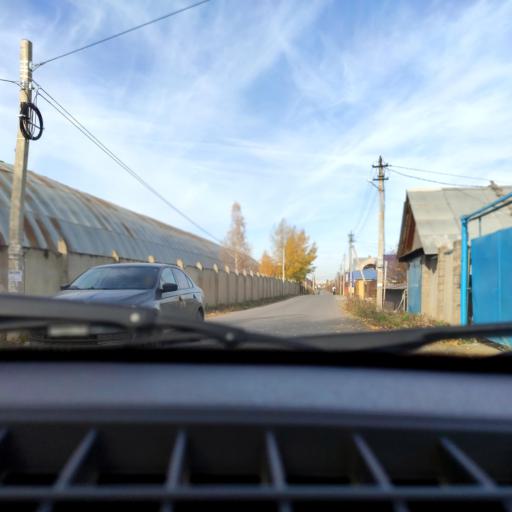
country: RU
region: Bashkortostan
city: Ufa
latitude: 54.6387
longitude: 55.9225
